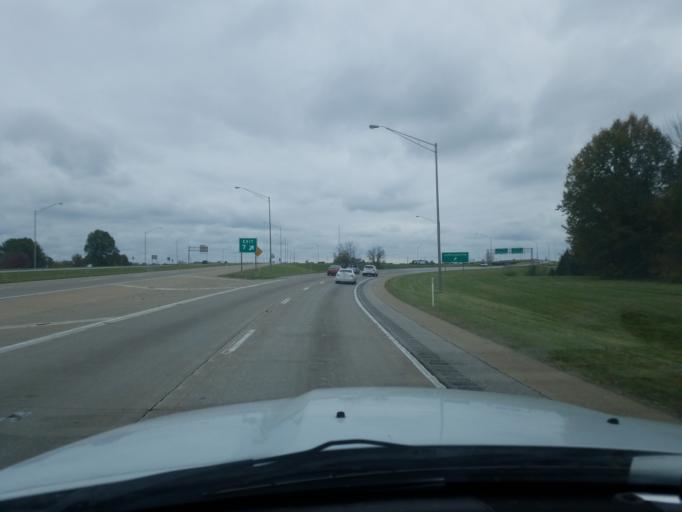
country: US
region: Indiana
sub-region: Clark County
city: Clarksville
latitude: 38.3454
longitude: -85.7593
